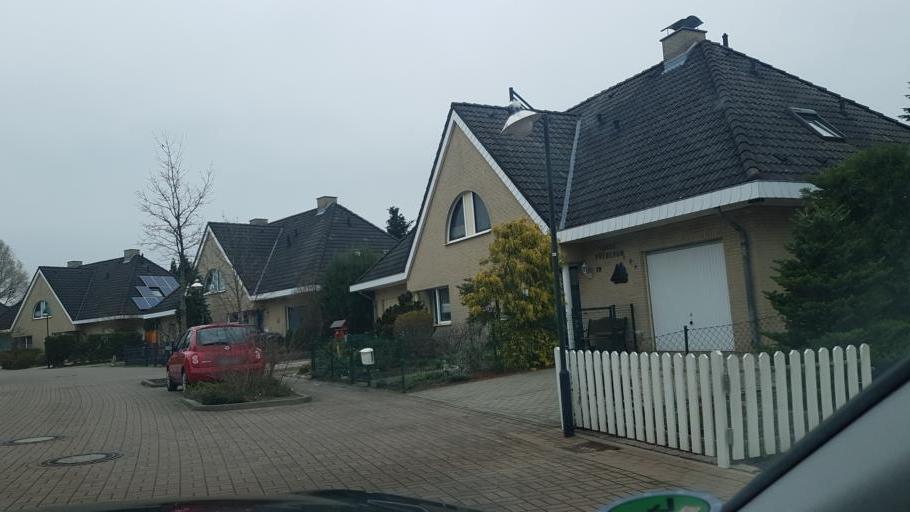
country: DE
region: Brandenburg
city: Mittenwalde
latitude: 52.2854
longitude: 13.5401
